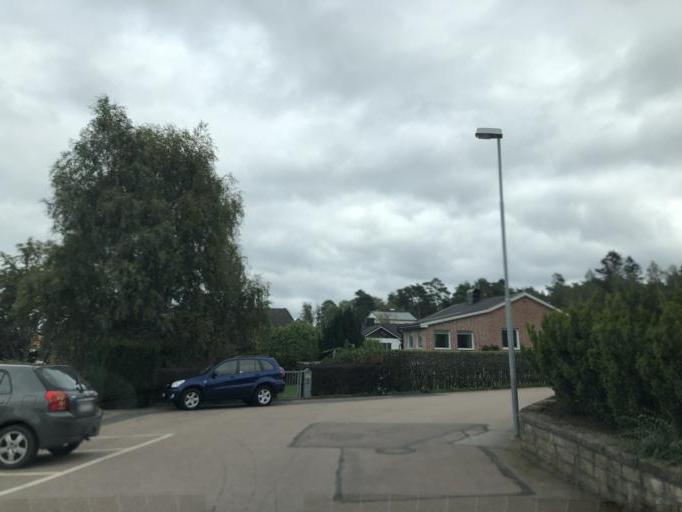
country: SE
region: Vaestra Goetaland
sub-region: Goteborg
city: Majorna
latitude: 57.7419
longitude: 11.8917
